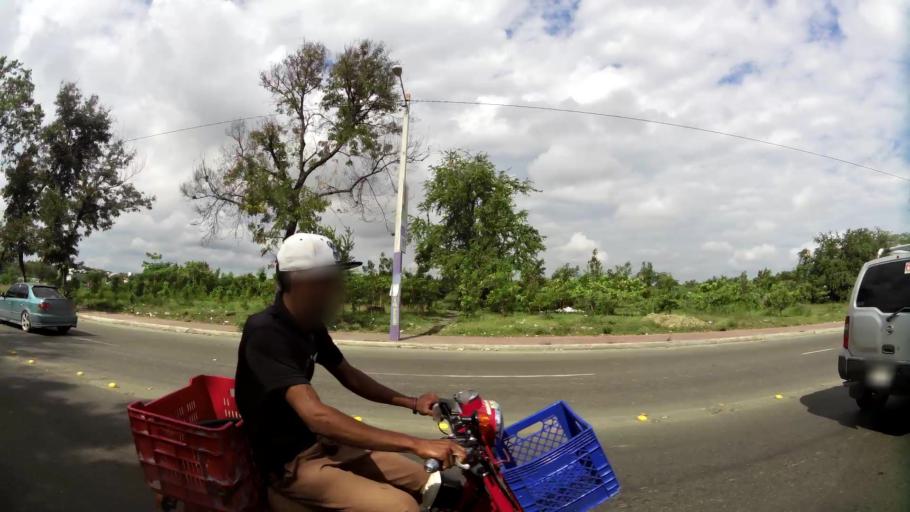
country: DO
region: Santiago
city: Santiago de los Caballeros
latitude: 19.4577
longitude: -70.7149
